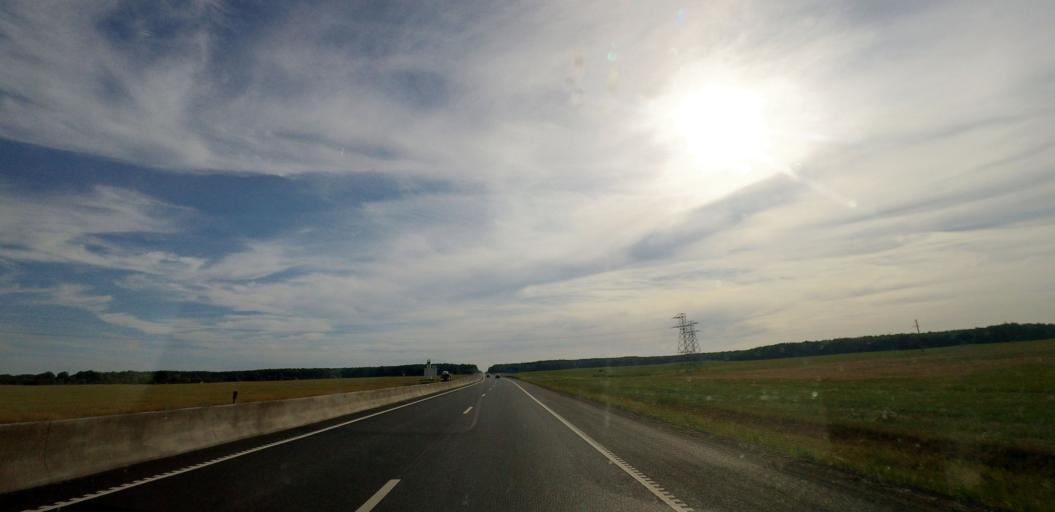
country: BY
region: Grodnenskaya
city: Shchuchin
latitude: 53.7128
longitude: 24.9442
